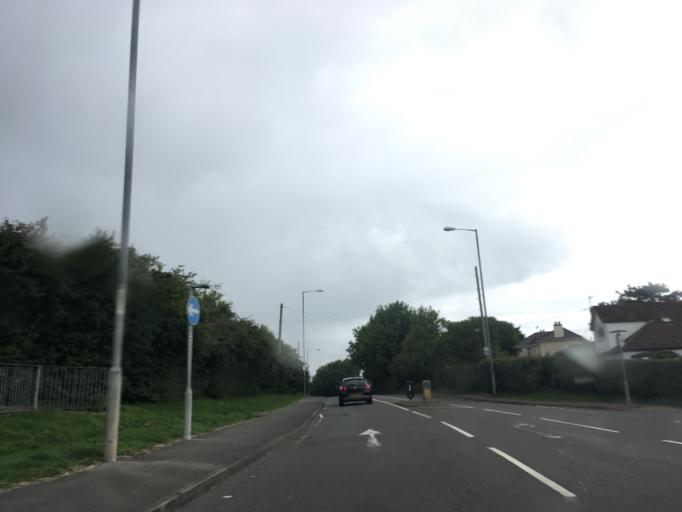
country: GB
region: Wales
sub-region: Monmouthshire
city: Chepstow
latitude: 51.6435
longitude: -2.6895
